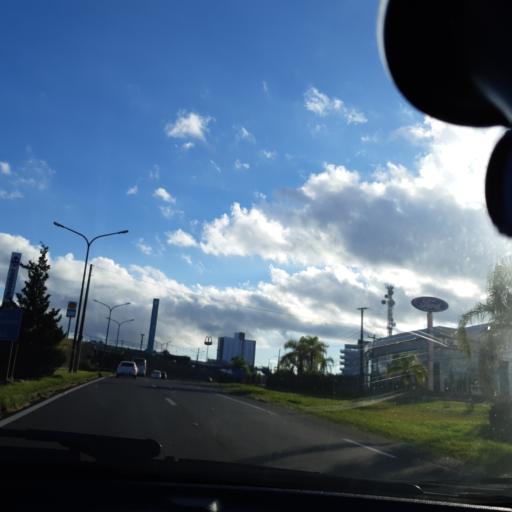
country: BR
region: Rio Grande do Sul
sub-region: Caxias Do Sul
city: Caxias do Sul
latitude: -29.1754
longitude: -51.2146
